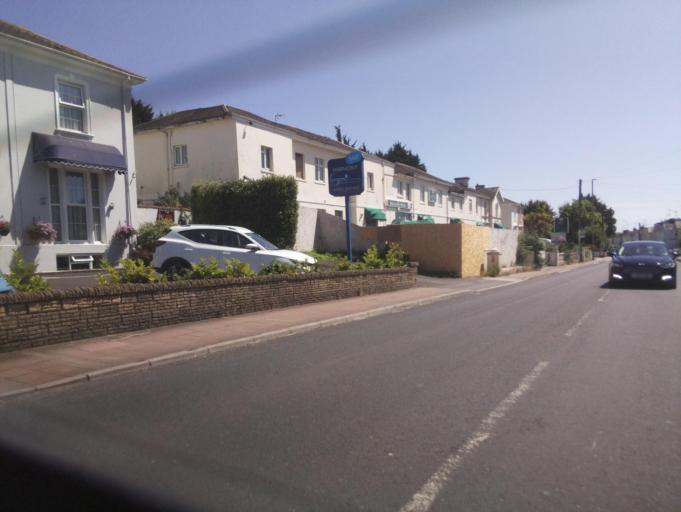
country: GB
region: England
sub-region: Borough of Torbay
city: Torquay
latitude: 50.4702
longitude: -3.5445
